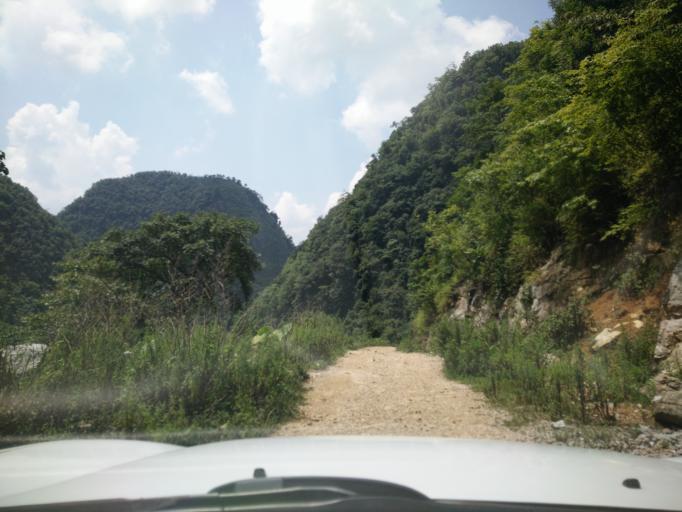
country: CN
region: Guangxi Zhuangzu Zizhiqu
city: Xinzhou
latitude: 25.0126
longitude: 105.7058
